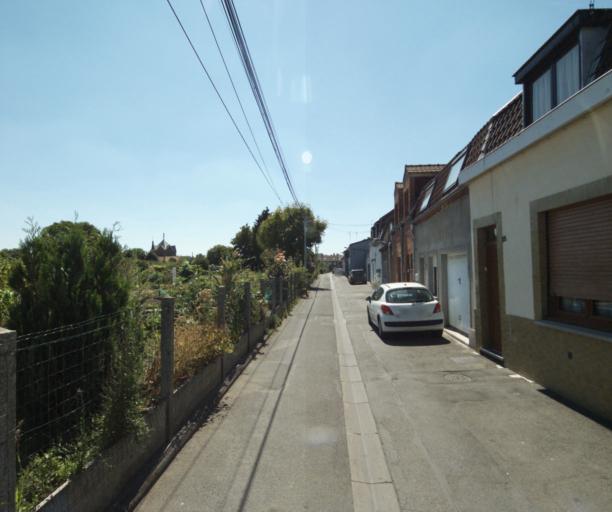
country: BE
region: Wallonia
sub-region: Province du Hainaut
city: Mouscron
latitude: 50.7375
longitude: 3.1949
